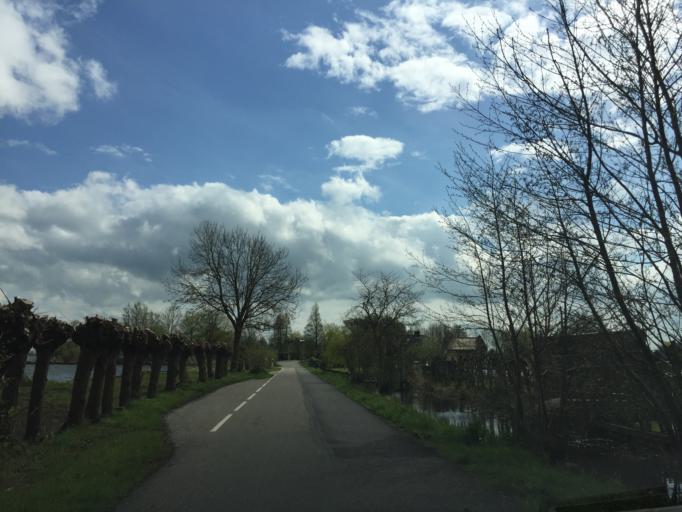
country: NL
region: South Holland
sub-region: Bodegraven-Reeuwijk
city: Reeuwijk
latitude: 52.0358
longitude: 4.7531
